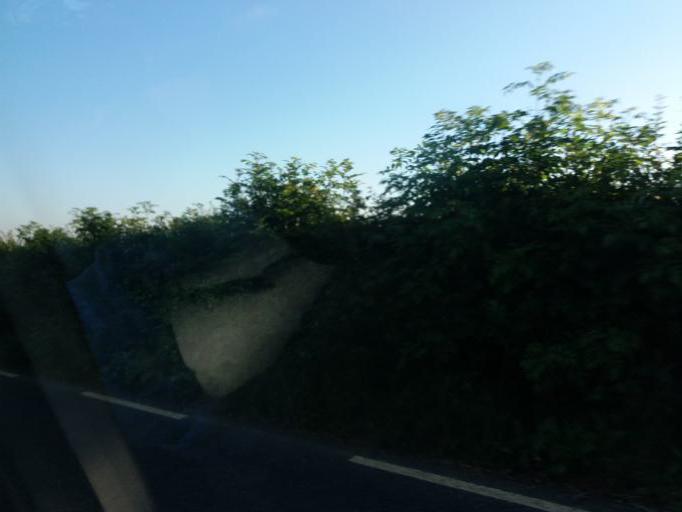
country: IE
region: Leinster
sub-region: An Mhi
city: Ashbourne
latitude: 53.5337
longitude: -6.3648
